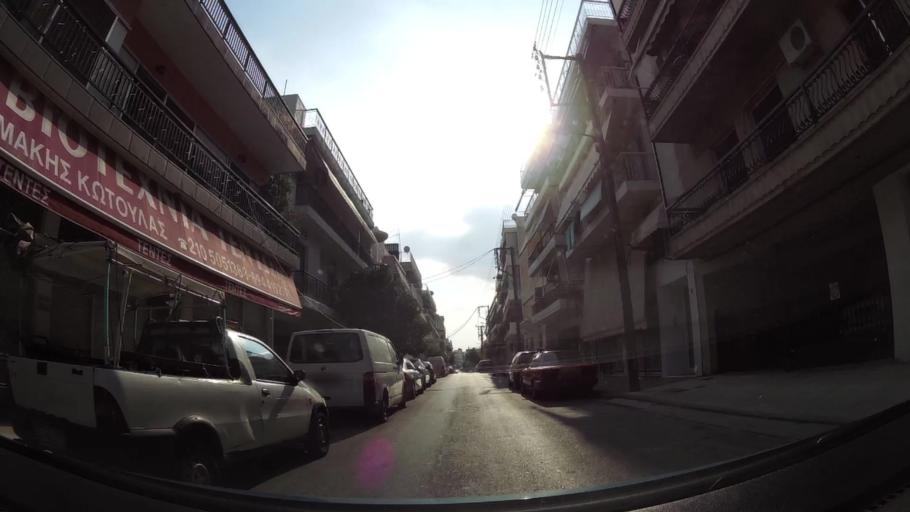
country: GR
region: Attica
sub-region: Nomarchia Athinas
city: Kamateron
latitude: 38.0459
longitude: 23.6978
